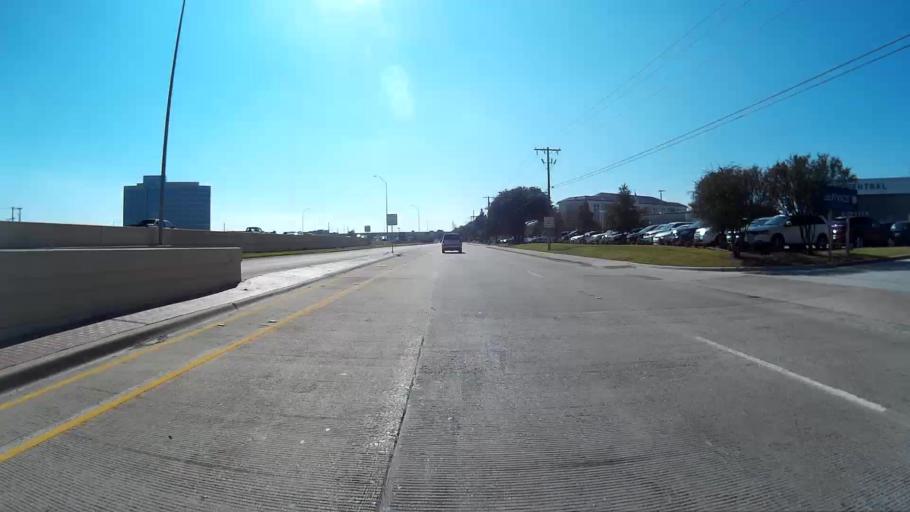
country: US
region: Texas
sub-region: Dallas County
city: Richardson
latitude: 32.9724
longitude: -96.7184
